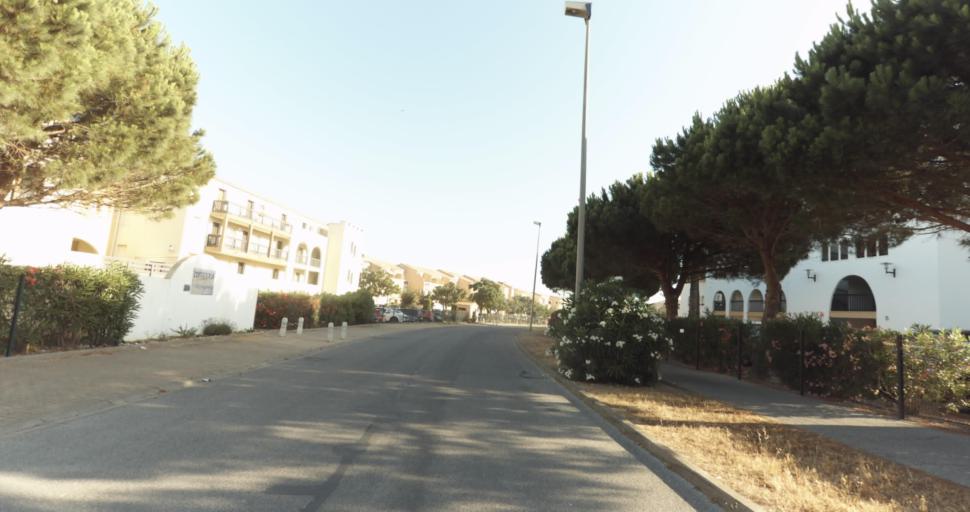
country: FR
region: Languedoc-Roussillon
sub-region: Departement des Pyrenees-Orientales
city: Saint-Cyprien-Plage
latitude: 42.6050
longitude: 3.0392
